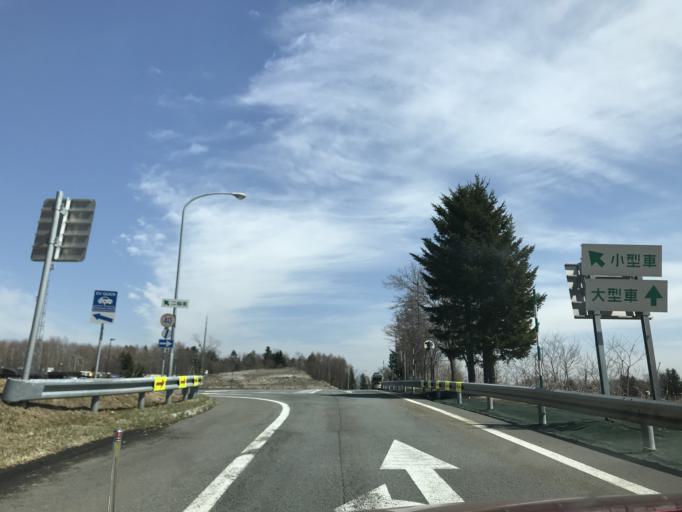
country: JP
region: Hokkaido
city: Iwamizawa
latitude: 43.1940
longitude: 141.8007
